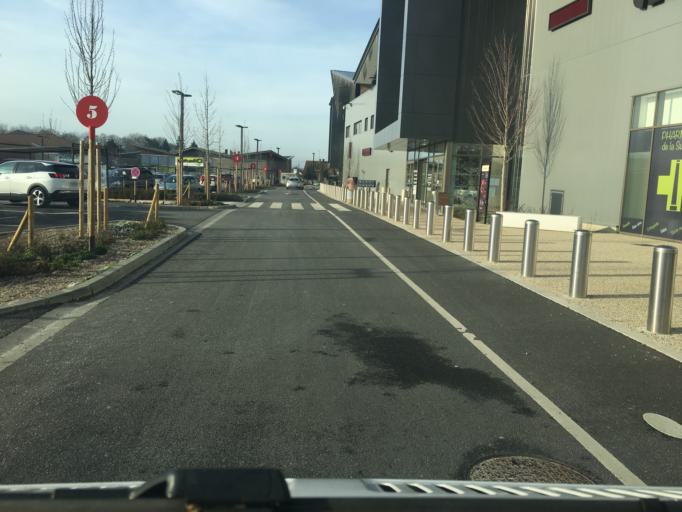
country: FR
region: Picardie
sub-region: Departement de la Somme
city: Abbeville
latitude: 50.1164
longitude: 1.8268
